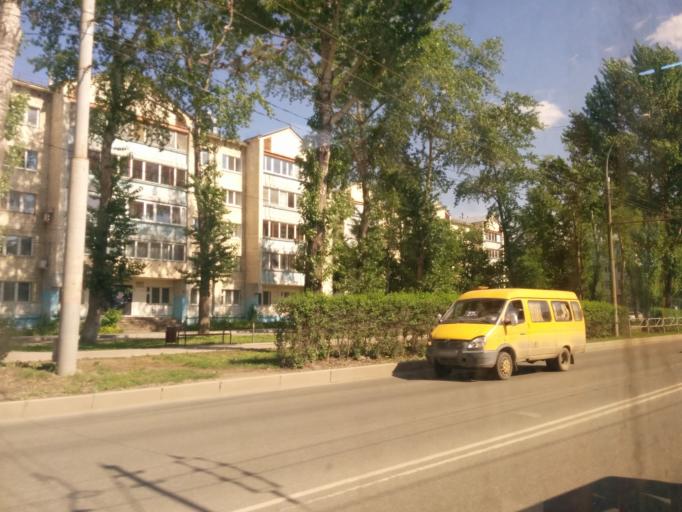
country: RU
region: Perm
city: Perm
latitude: 58.0116
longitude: 56.2799
